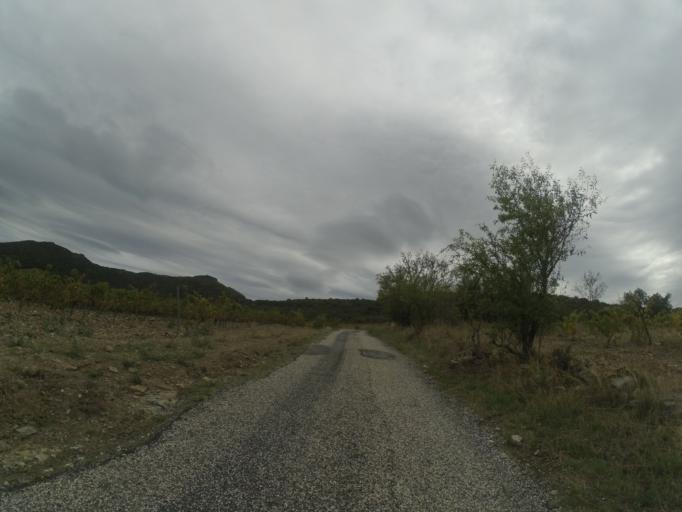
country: FR
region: Languedoc-Roussillon
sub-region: Departement des Pyrenees-Orientales
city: Millas
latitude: 42.7304
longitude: 2.6751
